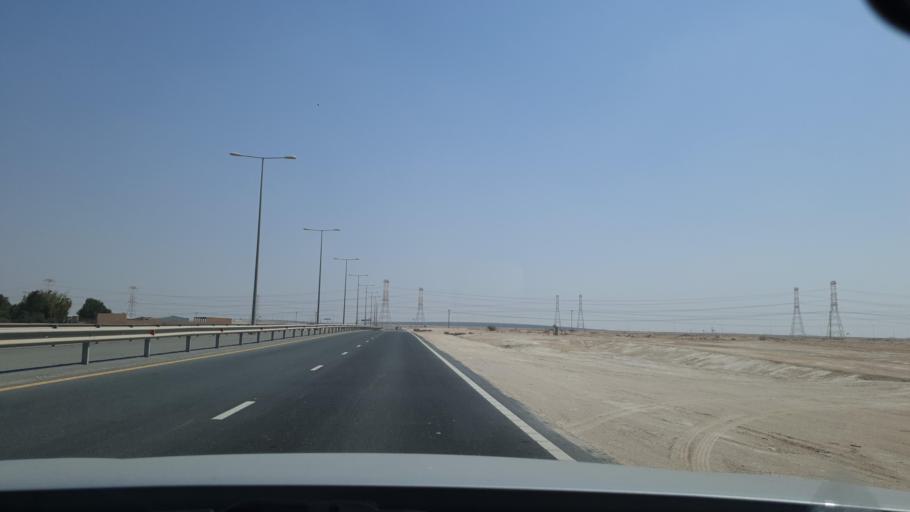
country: QA
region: Baladiyat az Za`ayin
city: Az Za`ayin
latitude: 25.6216
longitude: 51.3472
